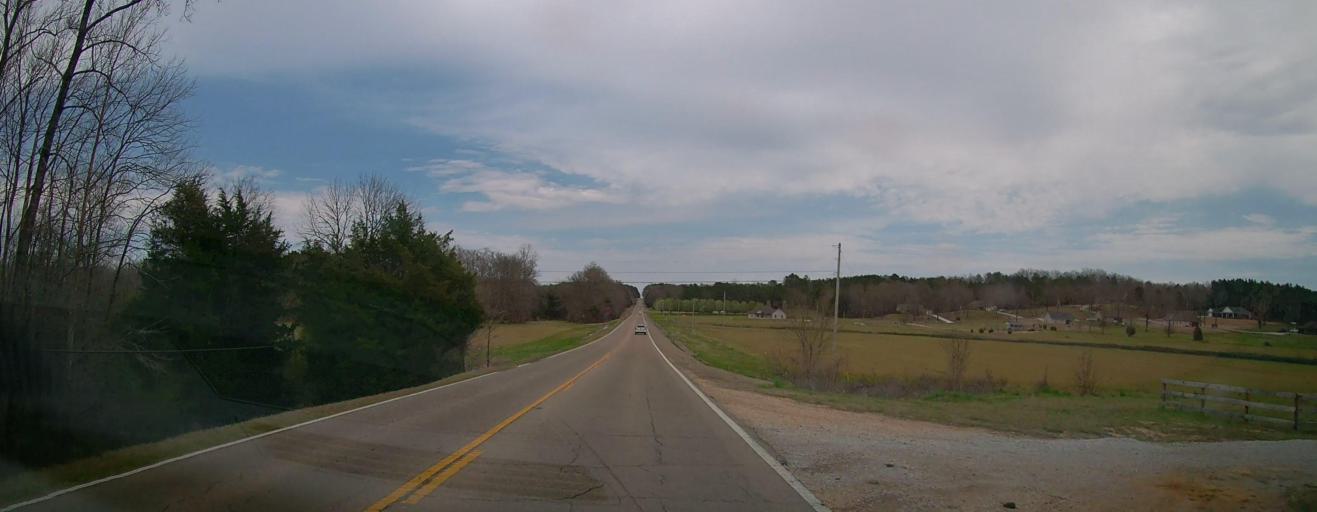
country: US
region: Mississippi
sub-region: Lee County
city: Plantersville
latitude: 34.2661
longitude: -88.6089
